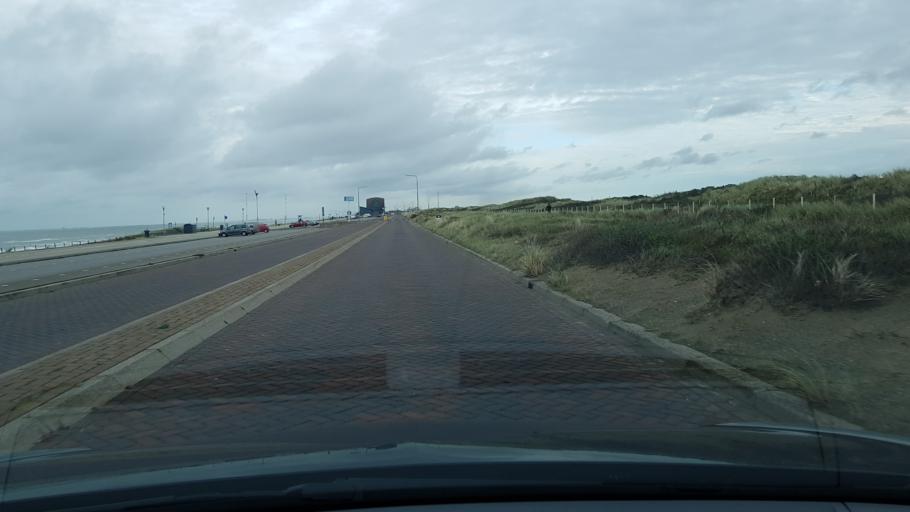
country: NL
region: North Holland
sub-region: Gemeente Zandvoort
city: Zandvoort
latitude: 52.3954
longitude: 4.5401
